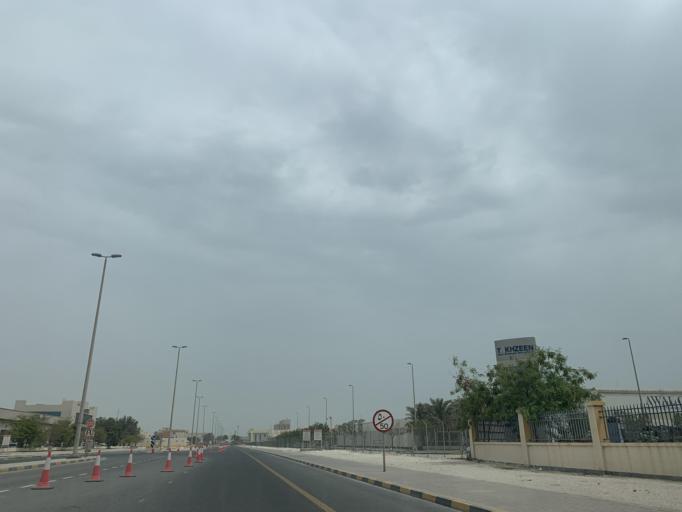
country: BH
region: Muharraq
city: Al Hadd
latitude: 26.2155
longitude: 50.6675
